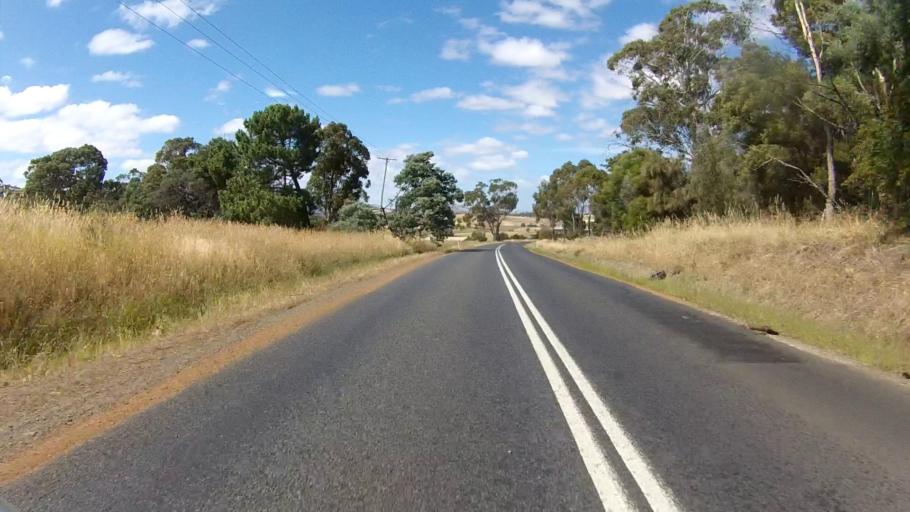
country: AU
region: Tasmania
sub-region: Sorell
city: Sorell
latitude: -42.6177
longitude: 147.4294
